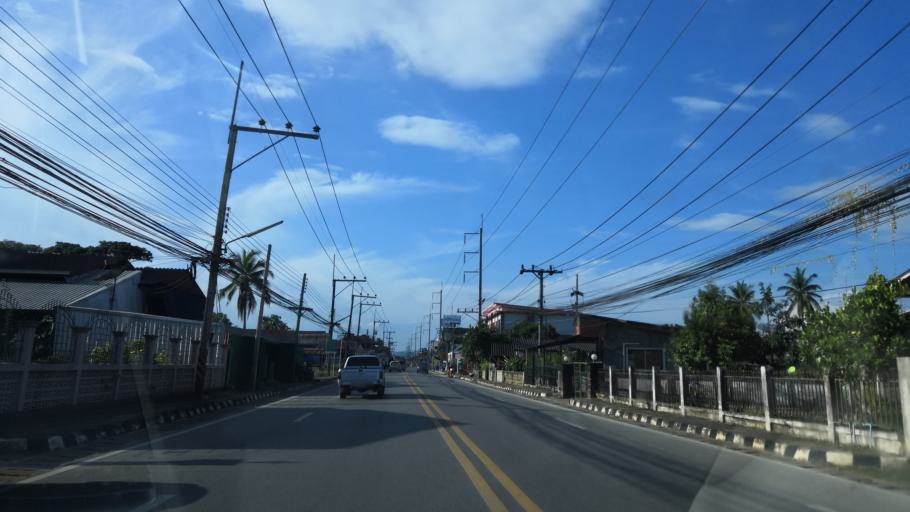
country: TH
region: Chiang Rai
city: Wiang Pa Pao
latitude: 19.3517
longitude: 99.5068
